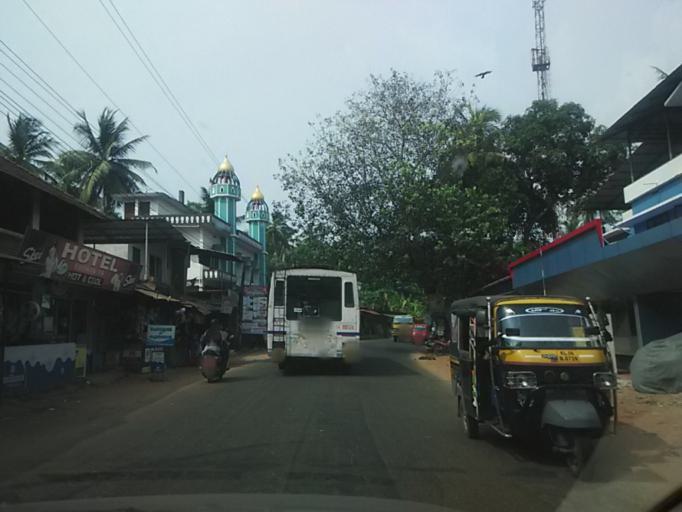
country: IN
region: Kerala
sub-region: Kozhikode
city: Naduvannur
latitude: 11.4691
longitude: 75.7726
